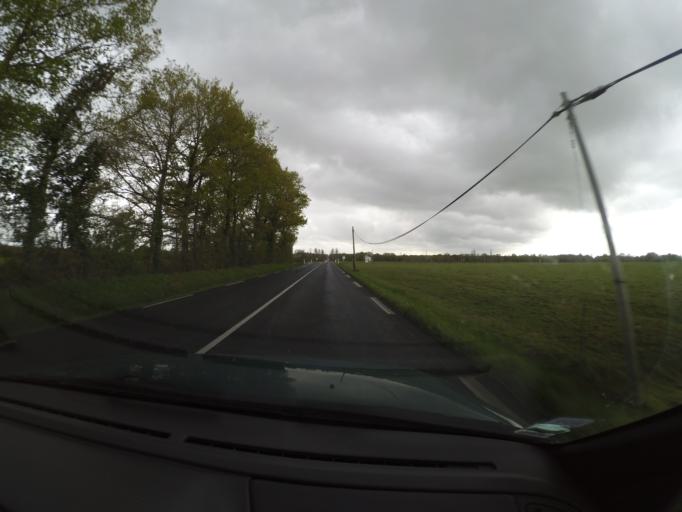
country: FR
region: Pays de la Loire
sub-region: Departement de la Loire-Atlantique
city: Vallet
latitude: 47.1959
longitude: -1.2491
